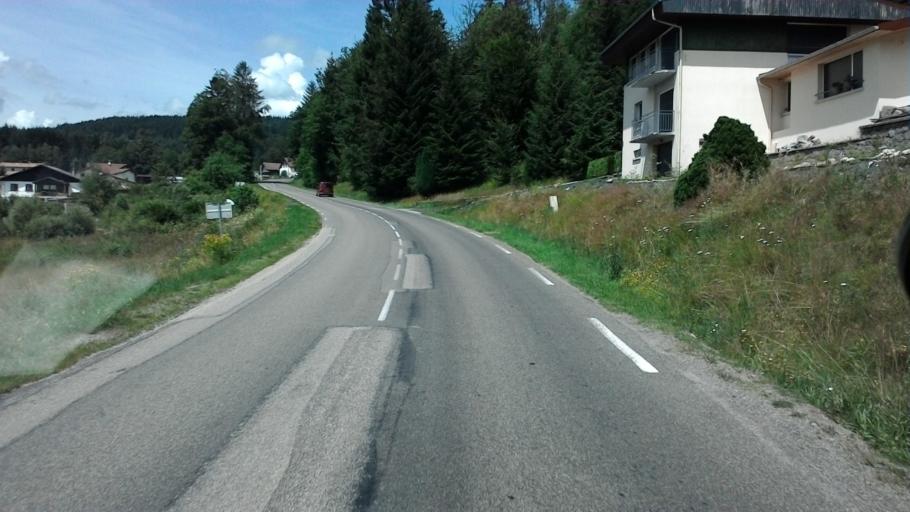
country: FR
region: Lorraine
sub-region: Departement des Vosges
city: Le Tholy
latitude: 48.0881
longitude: 6.7328
